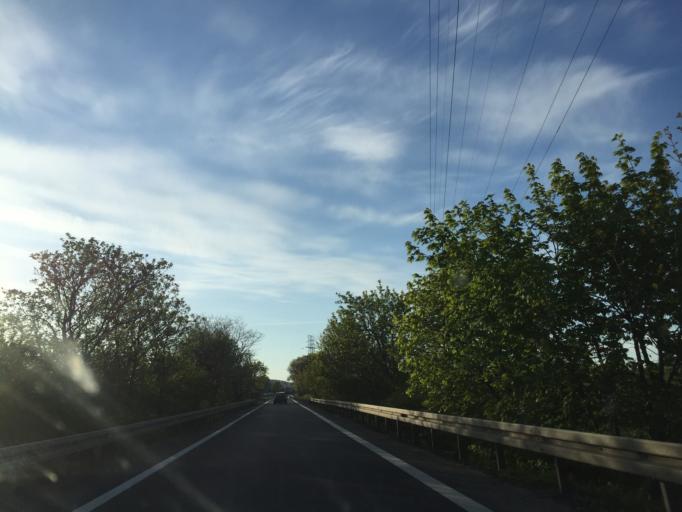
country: PL
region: Pomeranian Voivodeship
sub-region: Powiat gdanski
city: Kowale
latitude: 54.3252
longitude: 18.5436
